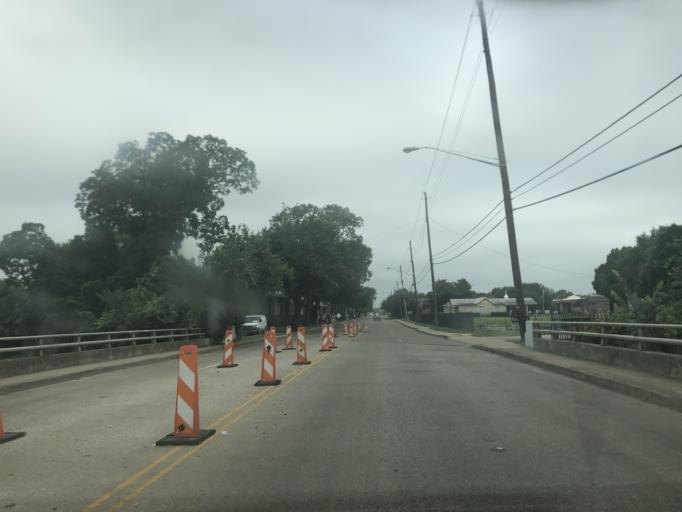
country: US
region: Texas
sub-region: Dallas County
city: Farmers Branch
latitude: 32.8665
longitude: -96.8696
